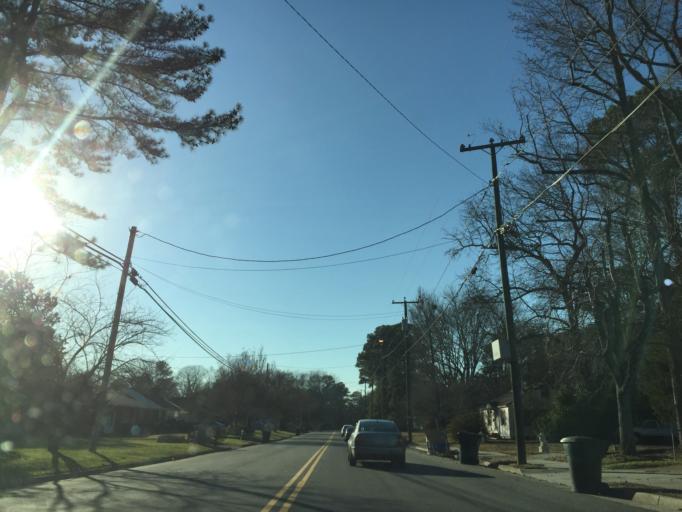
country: US
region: Virginia
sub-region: City of Newport News
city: Newport News
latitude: 37.0886
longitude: -76.5083
